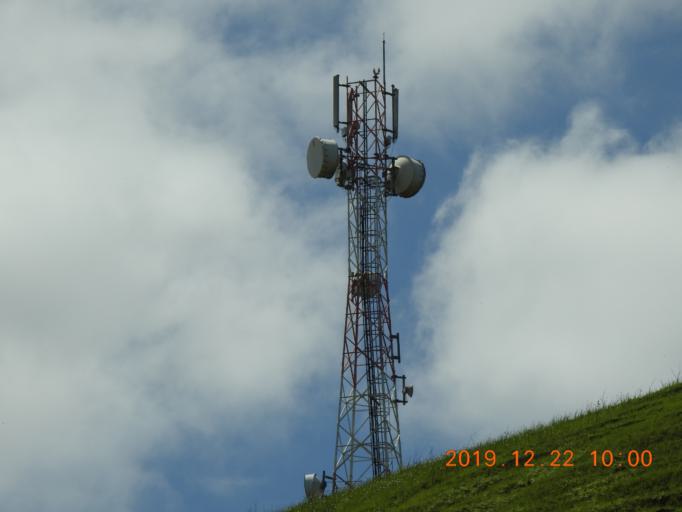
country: MG
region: Diana
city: Sadjoavato
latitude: -12.7011
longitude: 49.2526
